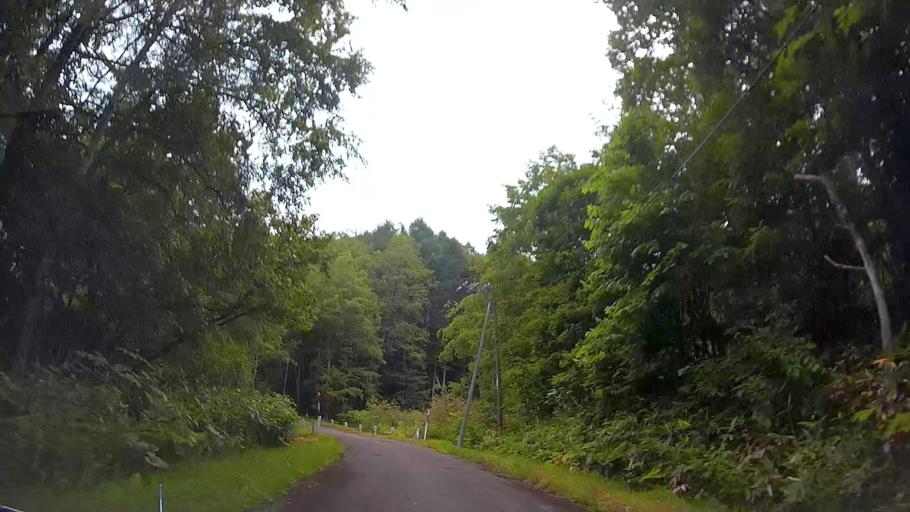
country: JP
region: Hokkaido
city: Nanae
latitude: 42.0669
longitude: 140.5027
